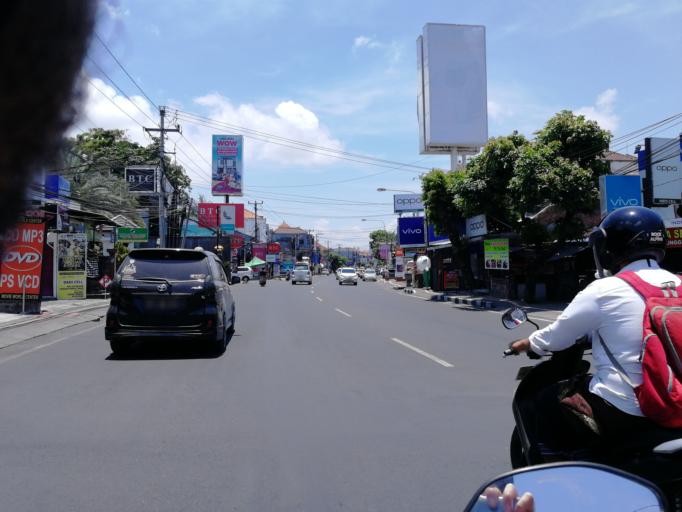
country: ID
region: Bali
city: Denpasar
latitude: -8.6742
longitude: 115.2077
